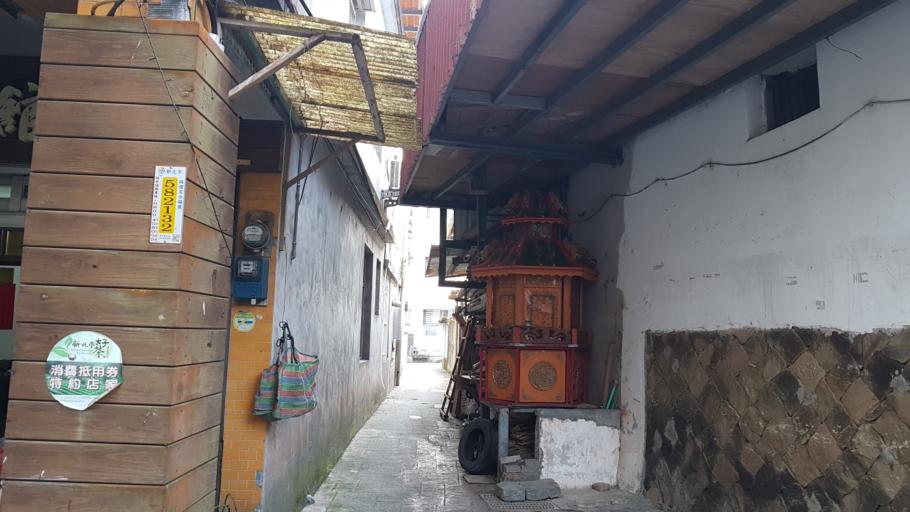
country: TW
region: Taiwan
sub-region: Yilan
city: Yilan
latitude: 24.9367
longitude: 121.7121
